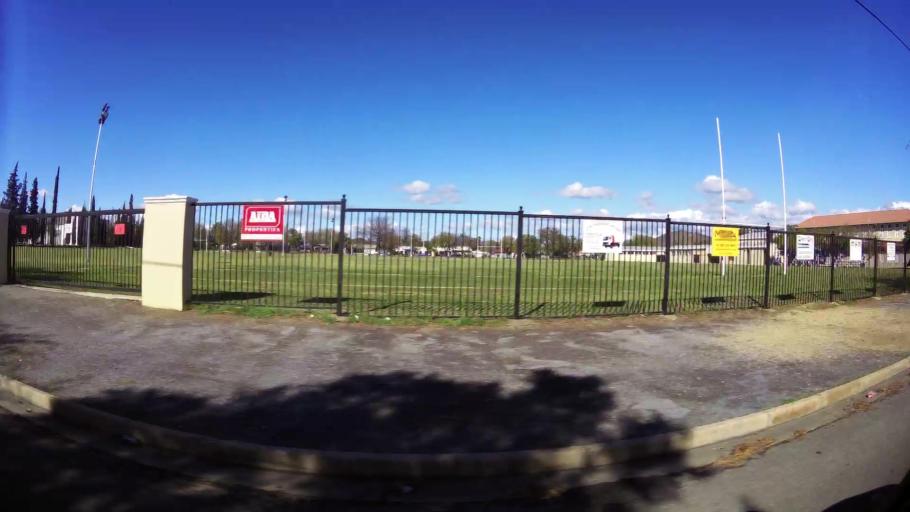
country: ZA
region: Western Cape
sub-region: Cape Winelands District Municipality
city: Ashton
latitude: -33.8048
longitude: 19.8899
